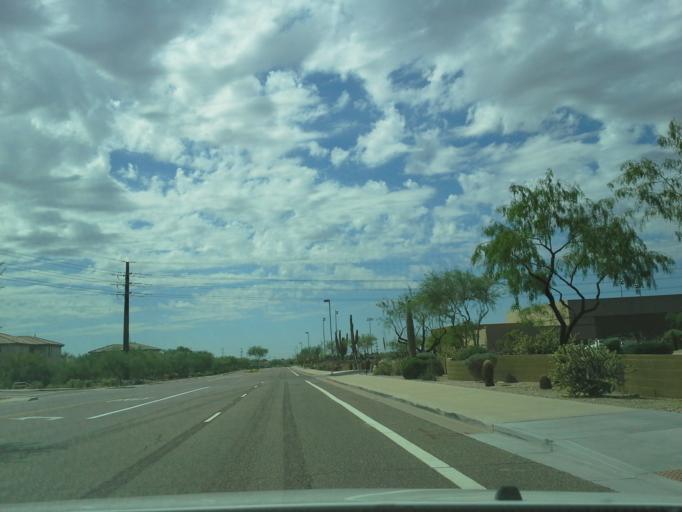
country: US
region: Arizona
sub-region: Maricopa County
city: Paradise Valley
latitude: 33.6371
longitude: -111.8699
